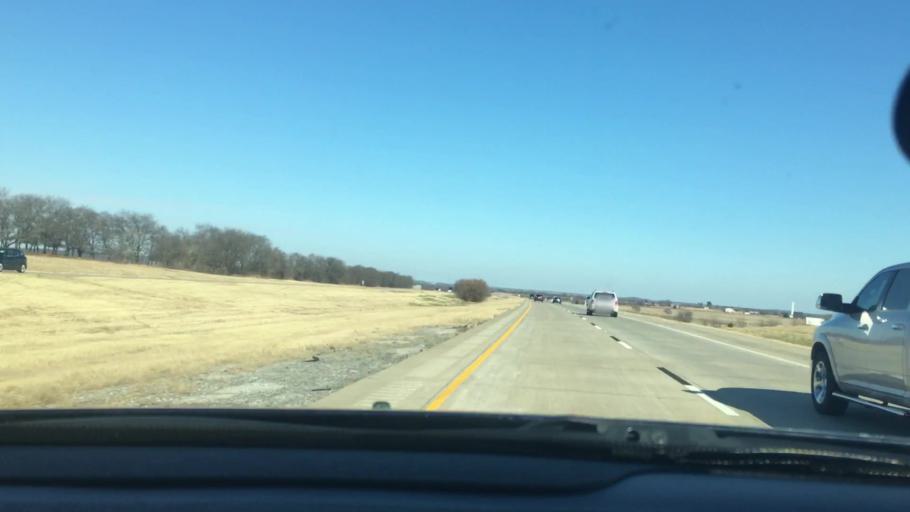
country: US
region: Oklahoma
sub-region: Love County
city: Marietta
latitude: 33.9624
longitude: -97.1339
